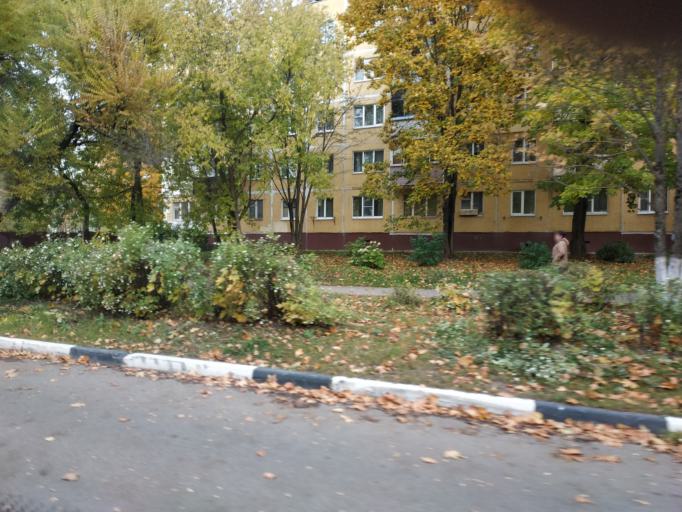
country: RU
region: Moskovskaya
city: Mozhaysk
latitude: 55.5017
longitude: 36.0338
